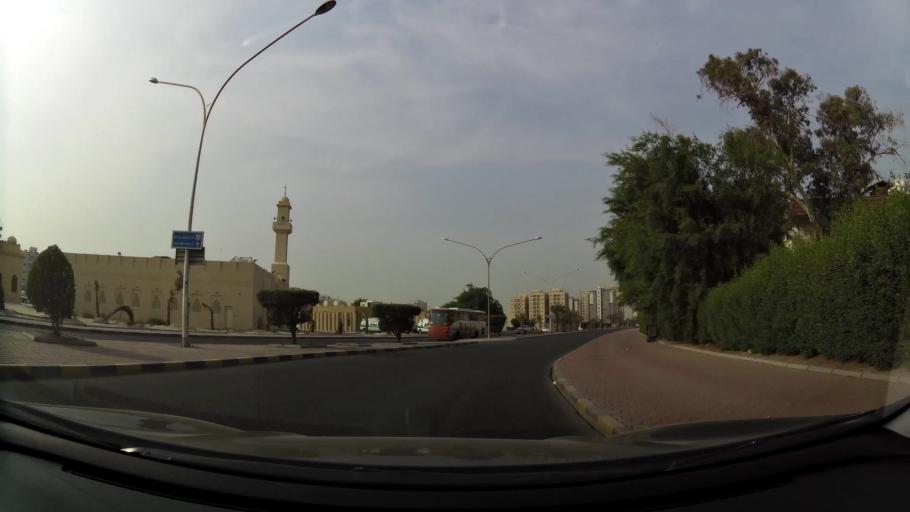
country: KW
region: Al Farwaniyah
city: Janub as Surrah
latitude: 29.2773
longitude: 47.9778
